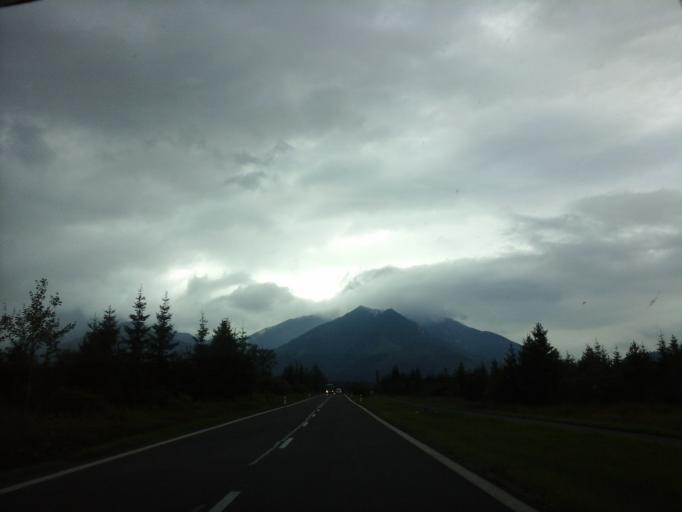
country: SK
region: Presovsky
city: Spisska Bela
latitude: 49.2118
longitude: 20.3636
